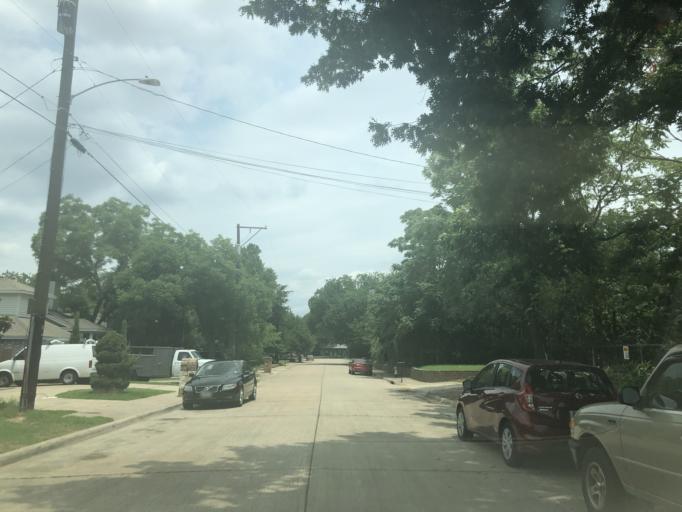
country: US
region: Texas
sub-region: Dallas County
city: Irving
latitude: 32.7971
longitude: -96.9370
